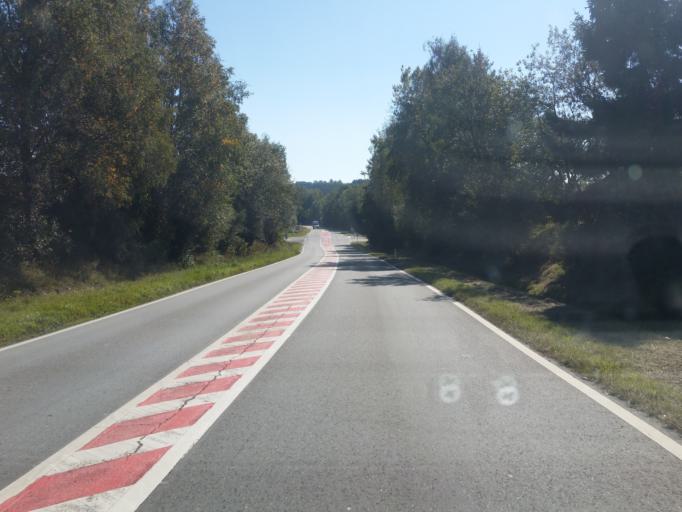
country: BE
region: Wallonia
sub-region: Province du Luxembourg
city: Bertrix
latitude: 49.8627
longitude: 5.2753
